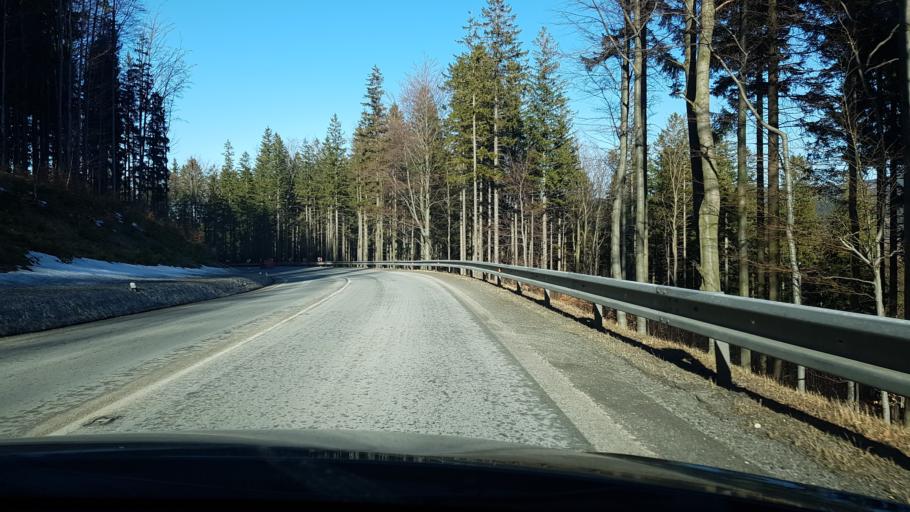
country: CZ
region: Olomoucky
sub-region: Okres Jesenik
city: Jesenik
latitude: 50.1468
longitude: 17.1689
